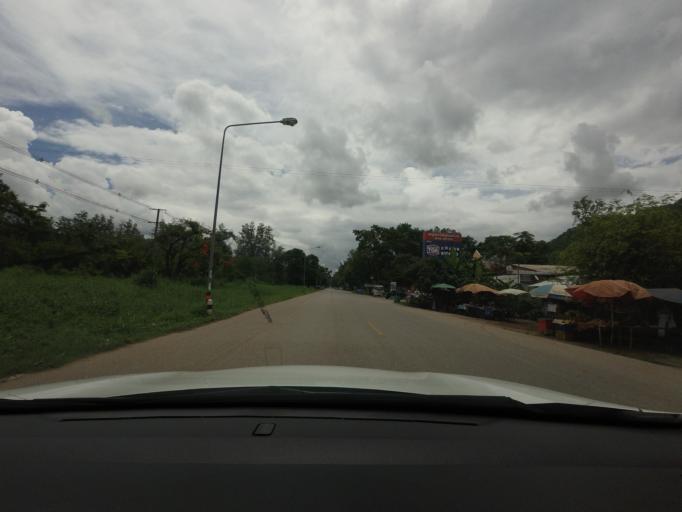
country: TH
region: Nakhon Ratchasima
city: Pak Chong
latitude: 14.5348
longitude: 101.3728
